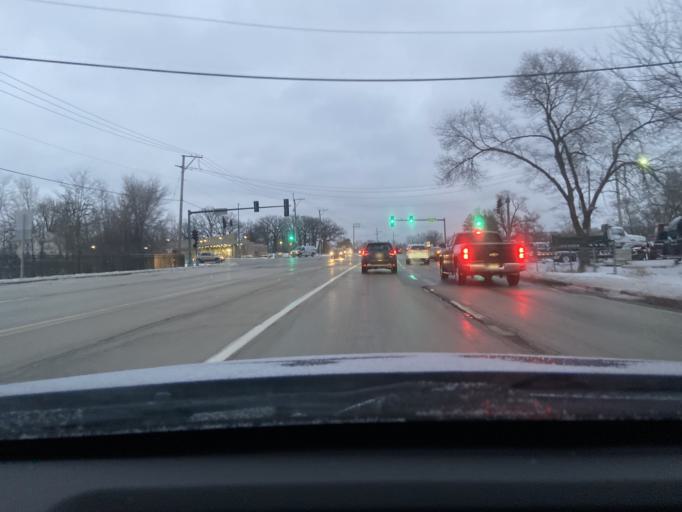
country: US
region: Illinois
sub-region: Lake County
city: Grayslake
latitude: 42.3598
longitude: -88.0343
